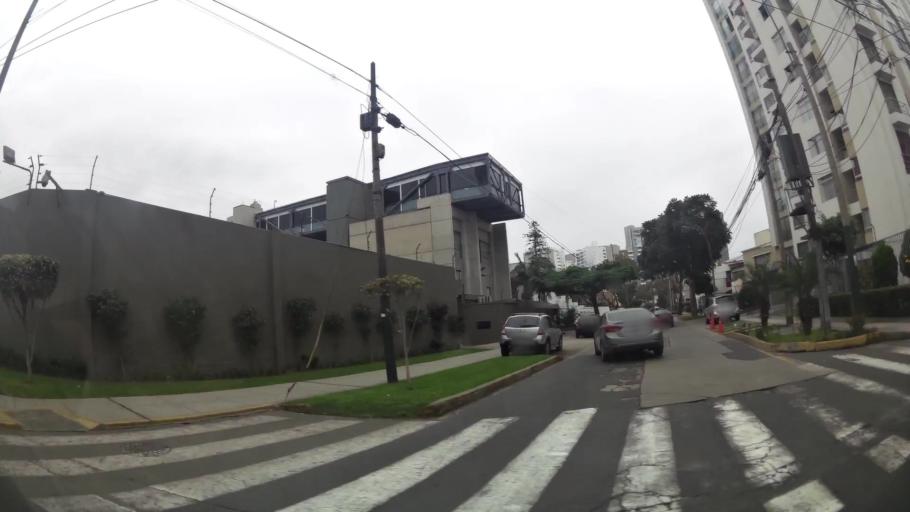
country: PE
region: Lima
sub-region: Lima
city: San Isidro
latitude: -12.0827
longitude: -77.0506
